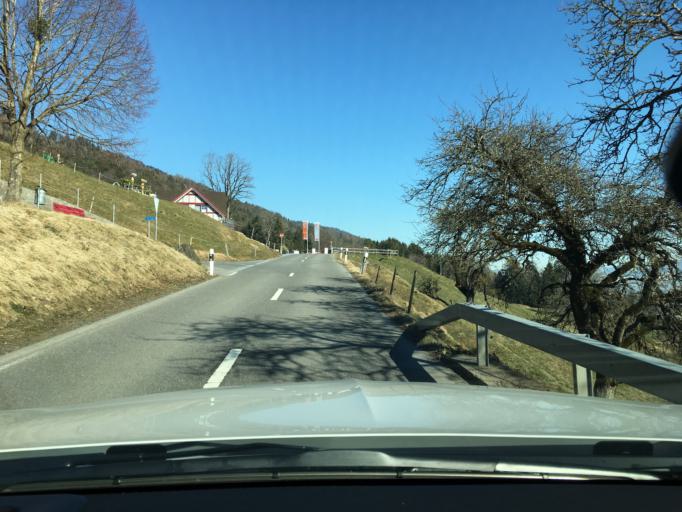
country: CH
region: Saint Gallen
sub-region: Wahlkreis Rheintal
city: Altstatten
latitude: 47.3934
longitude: 9.5536
